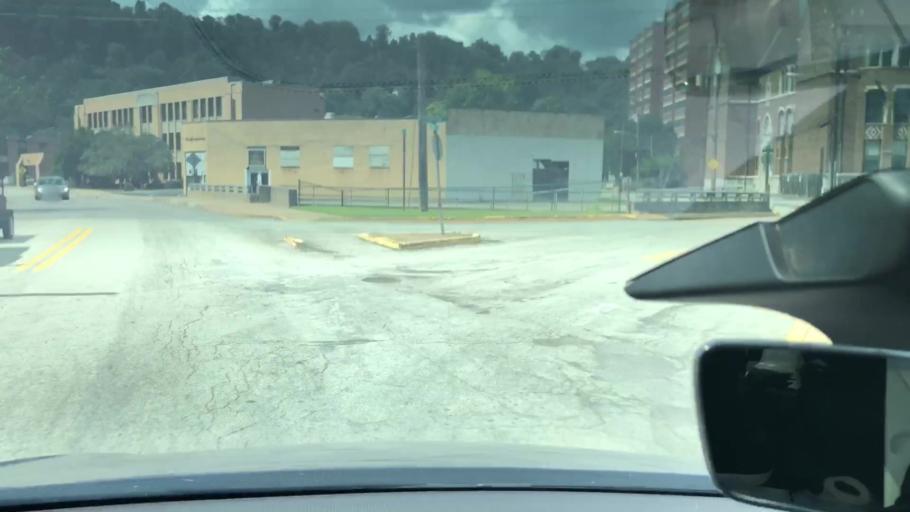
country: US
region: Pennsylvania
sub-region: Allegheny County
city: Turtle Creek
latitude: 40.4053
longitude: -79.8271
